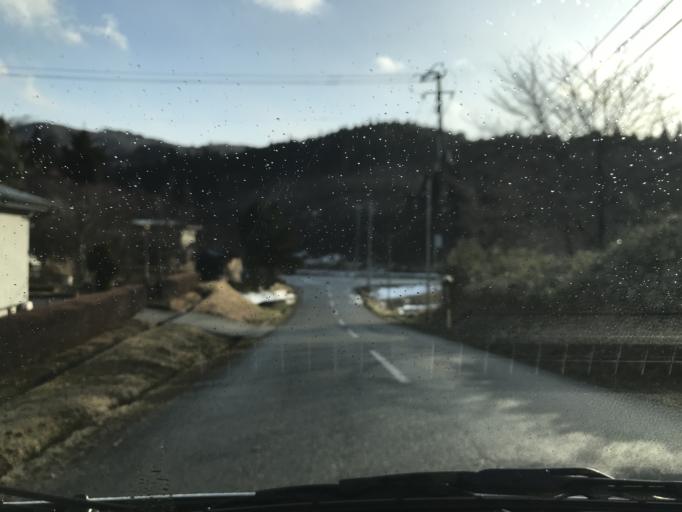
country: JP
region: Iwate
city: Mizusawa
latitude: 39.0789
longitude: 141.0030
